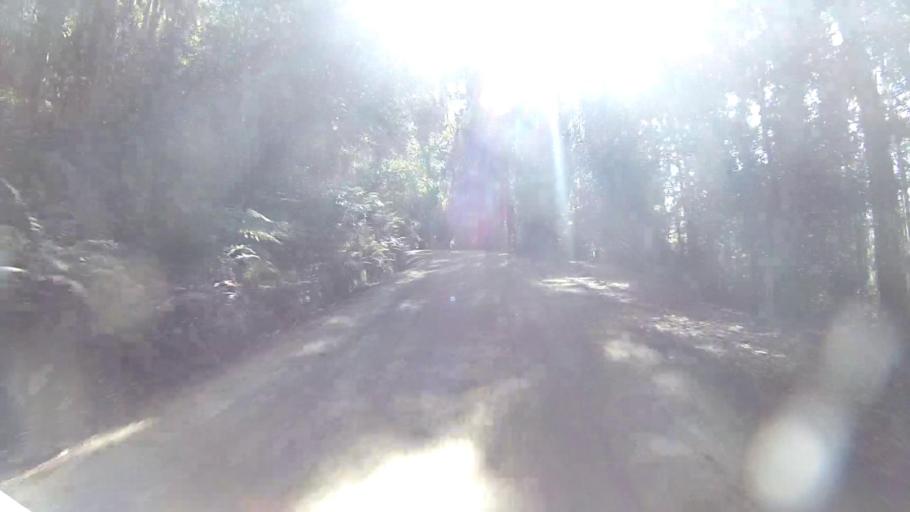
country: AU
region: Tasmania
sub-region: Derwent Valley
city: New Norfolk
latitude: -42.6769
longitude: 146.7027
